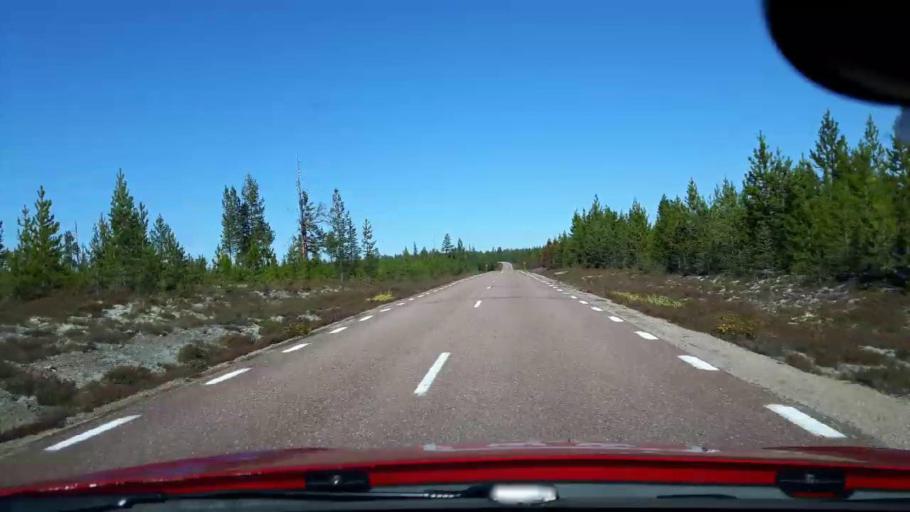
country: SE
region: Jaemtland
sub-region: Harjedalens Kommun
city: Sveg
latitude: 61.7132
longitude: 14.1687
